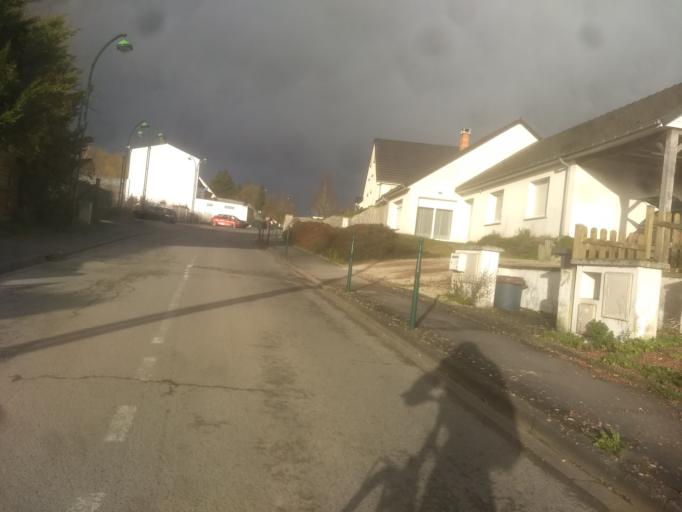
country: FR
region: Nord-Pas-de-Calais
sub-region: Departement du Pas-de-Calais
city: Saint-Laurent-Blangy
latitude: 50.3053
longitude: 2.8109
